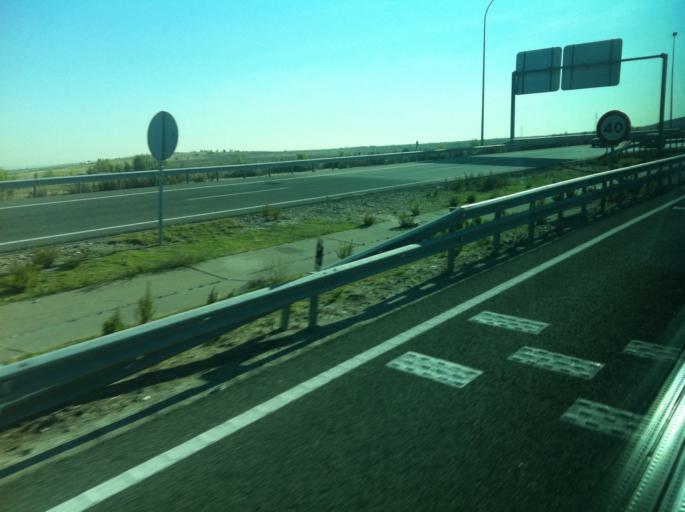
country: ES
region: Madrid
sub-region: Provincia de Madrid
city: San Sebastian de los Reyes
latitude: 40.5337
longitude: -3.5827
